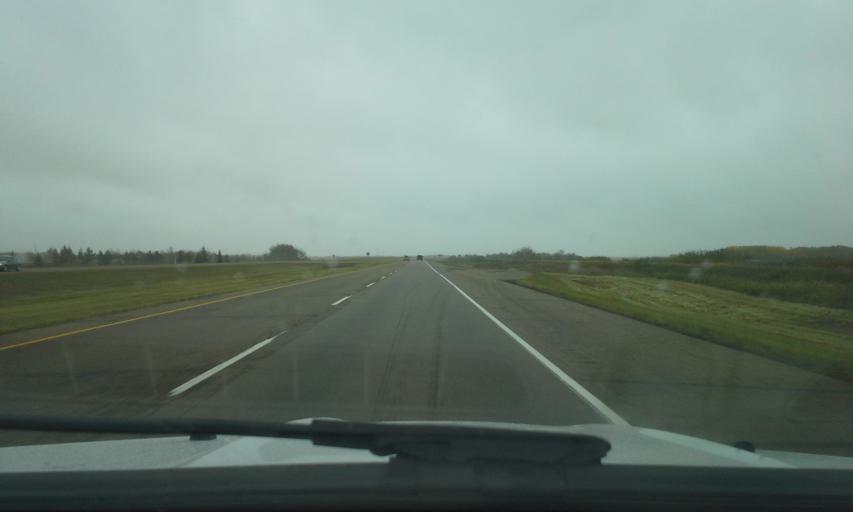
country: CA
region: Saskatchewan
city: Lloydminster
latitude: 53.2304
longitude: -109.8365
